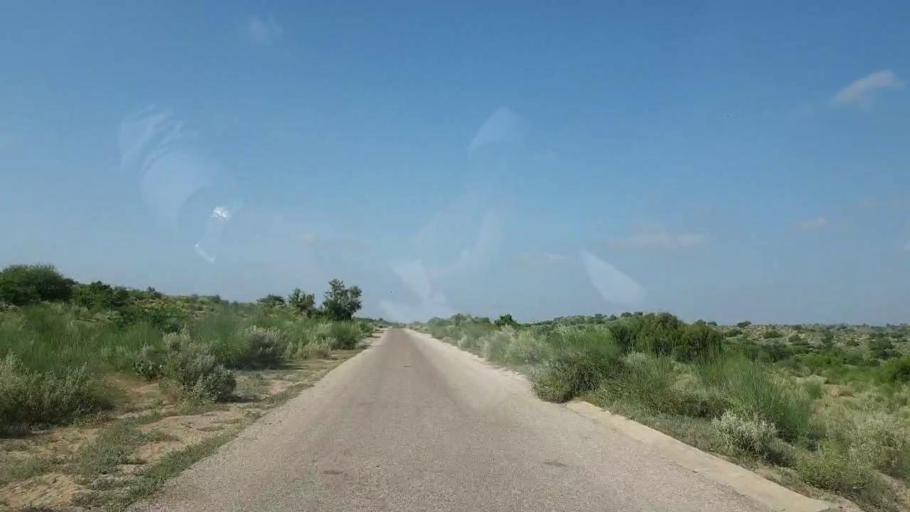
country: PK
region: Sindh
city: Mithi
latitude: 24.5664
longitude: 69.9146
